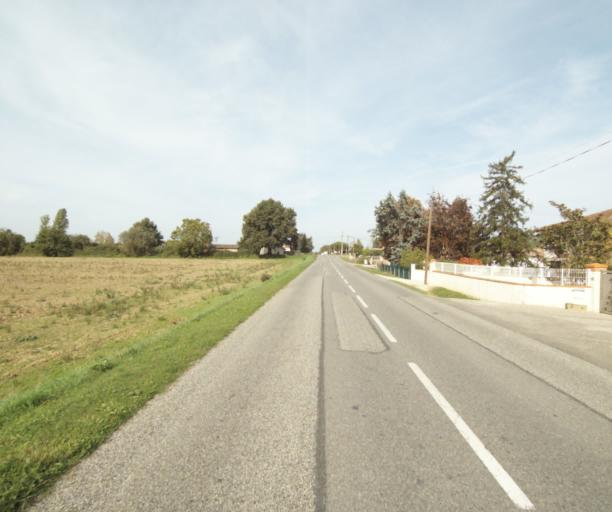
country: FR
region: Midi-Pyrenees
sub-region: Departement du Tarn-et-Garonne
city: Corbarieu
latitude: 43.9549
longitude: 1.3645
